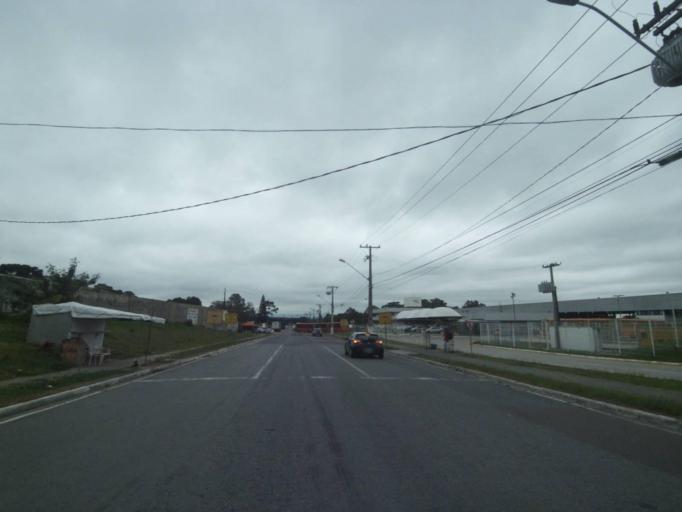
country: BR
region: Parana
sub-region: Sao Jose Dos Pinhais
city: Sao Jose dos Pinhais
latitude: -25.5411
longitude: -49.3089
